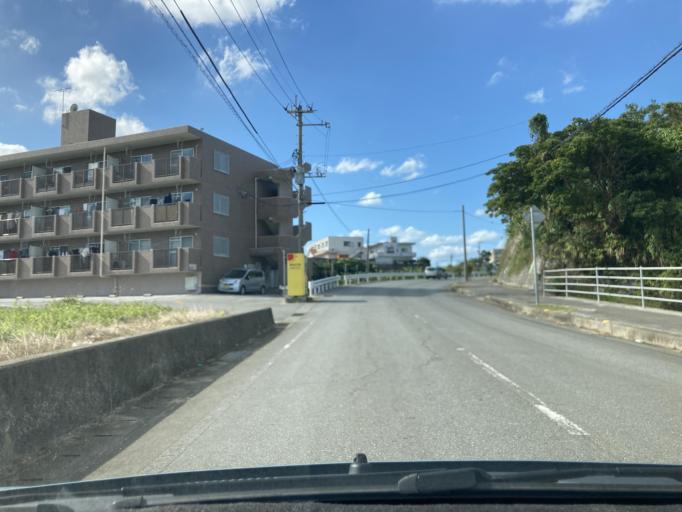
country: JP
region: Okinawa
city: Gushikawa
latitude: 26.3682
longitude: 127.8413
